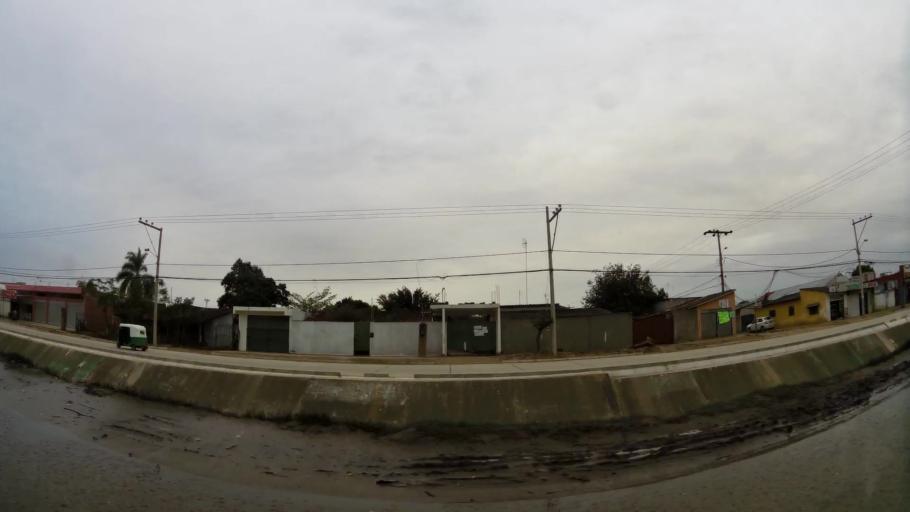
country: BO
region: Santa Cruz
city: Santa Cruz de la Sierra
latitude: -17.8593
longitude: -63.1750
